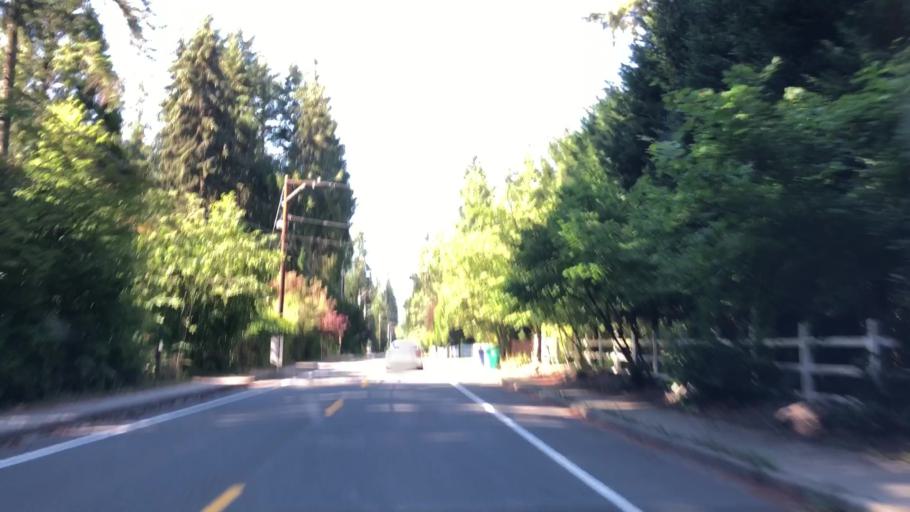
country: US
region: Washington
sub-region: King County
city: Woodinville
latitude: 47.7849
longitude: -122.1674
